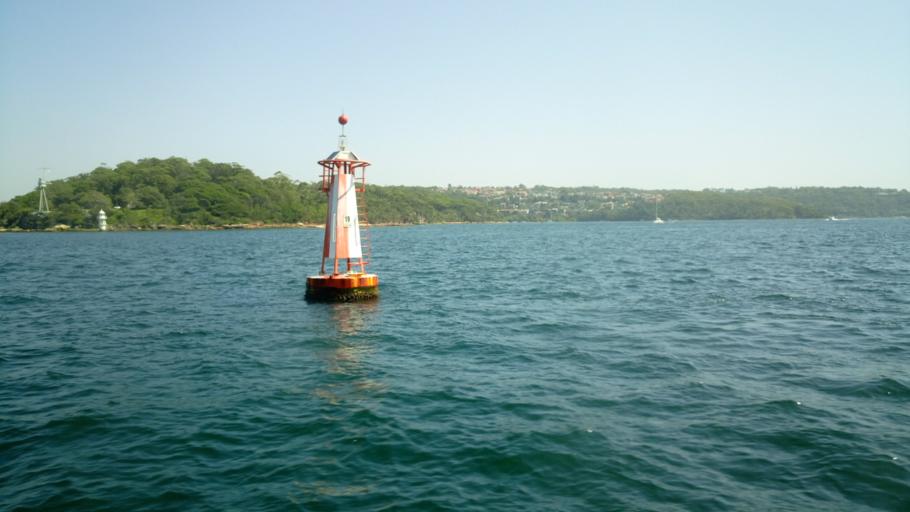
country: AU
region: New South Wales
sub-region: Woollahra
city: Point Piper
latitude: -33.8563
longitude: 151.2493
